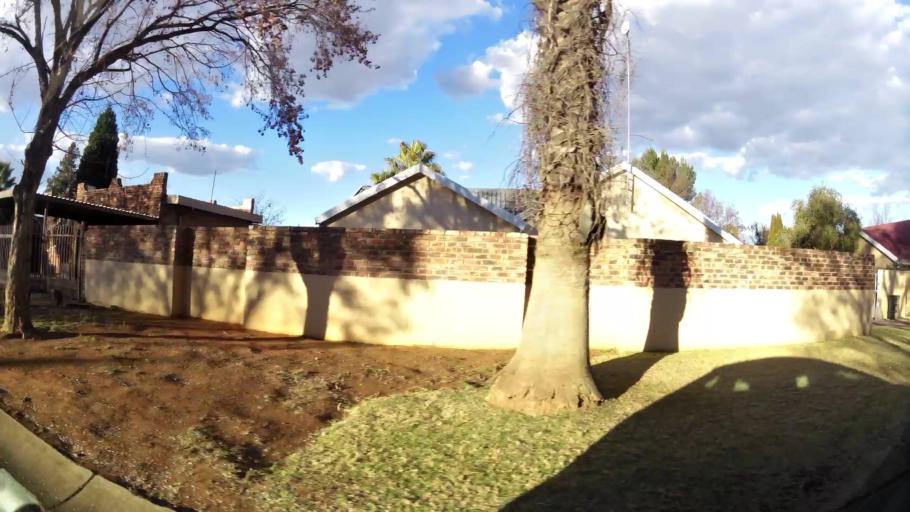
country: ZA
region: North-West
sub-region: Dr Kenneth Kaunda District Municipality
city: Potchefstroom
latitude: -26.7327
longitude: 27.0999
